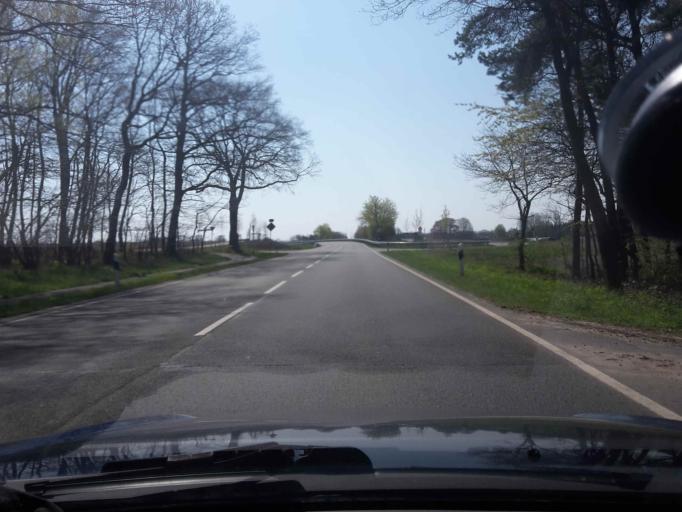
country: DE
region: Lower Saxony
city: Schneverdingen
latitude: 53.0903
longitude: 9.8598
